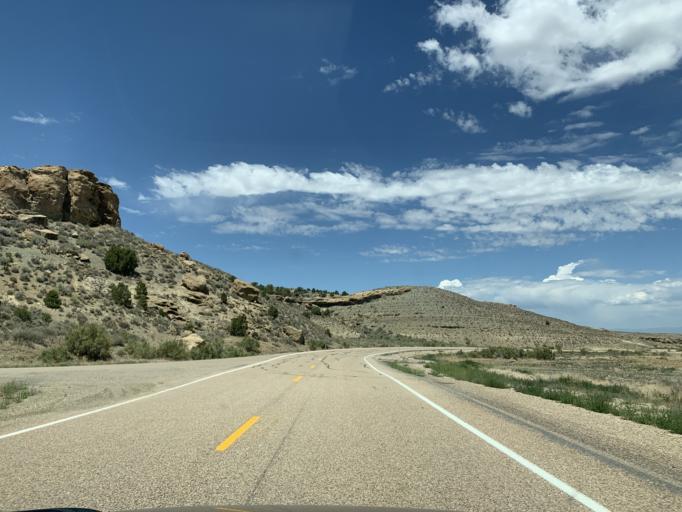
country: US
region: Utah
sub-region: Duchesne County
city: Duchesne
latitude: 40.0173
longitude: -110.1563
